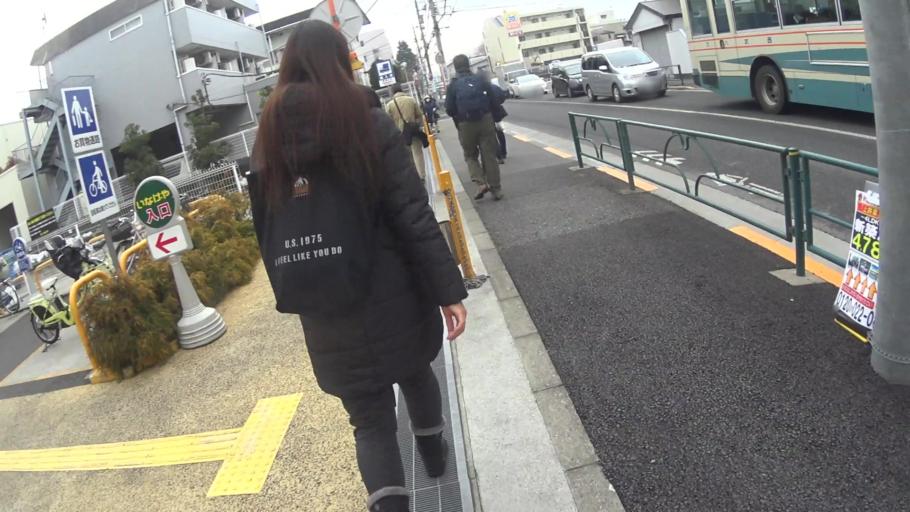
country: JP
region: Tokyo
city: Musashino
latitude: 35.7290
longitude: 139.6001
